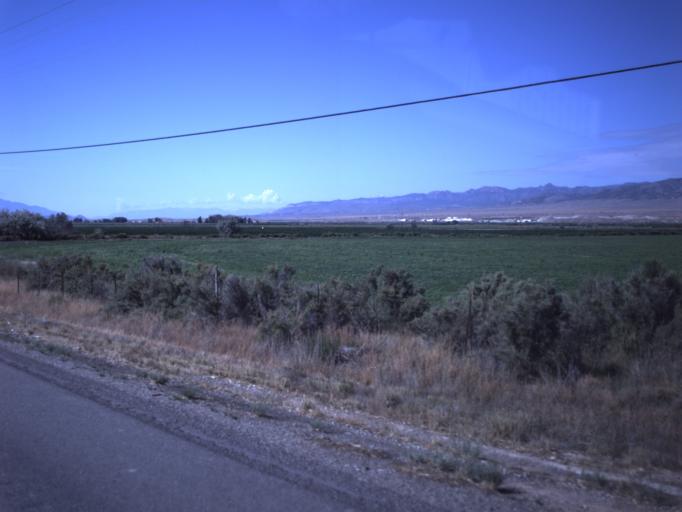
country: US
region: Utah
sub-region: Sanpete County
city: Centerfield
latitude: 39.0842
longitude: -111.8202
